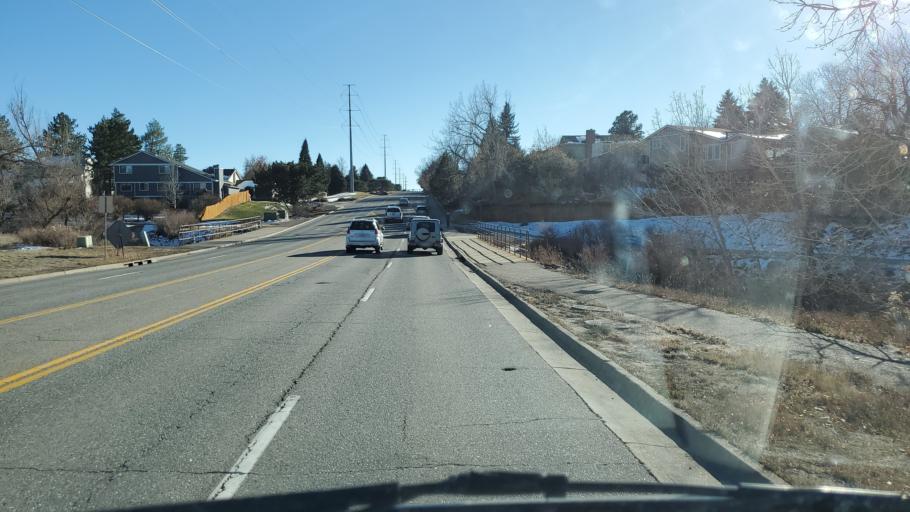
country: US
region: Colorado
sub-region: Arapahoe County
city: Castlewood
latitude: 39.5770
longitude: -104.9044
